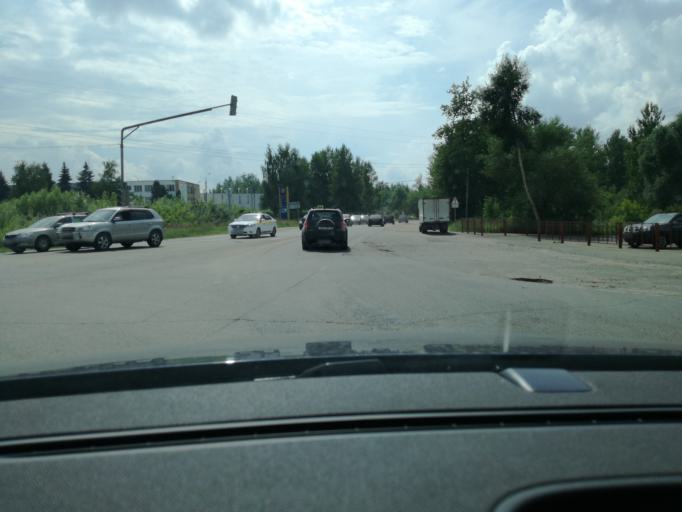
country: RU
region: Moskovskaya
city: Dmitrov
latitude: 56.3371
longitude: 37.5541
